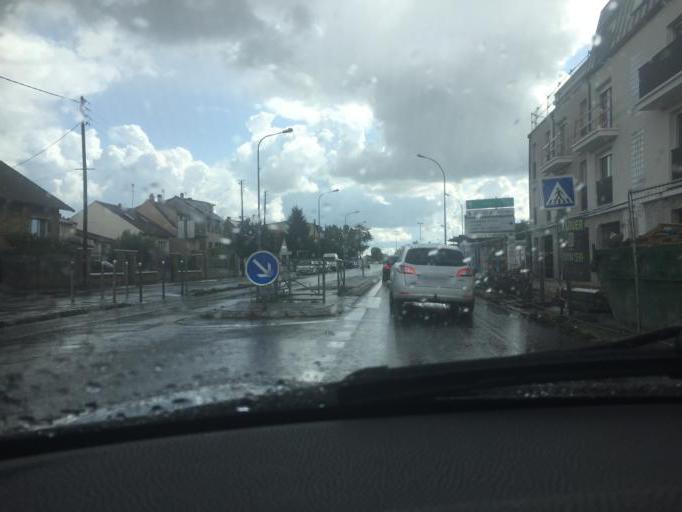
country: FR
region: Ile-de-France
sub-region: Departement du Val-de-Marne
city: Chennevieres-sur-Marne
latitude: 48.8007
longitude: 2.5420
